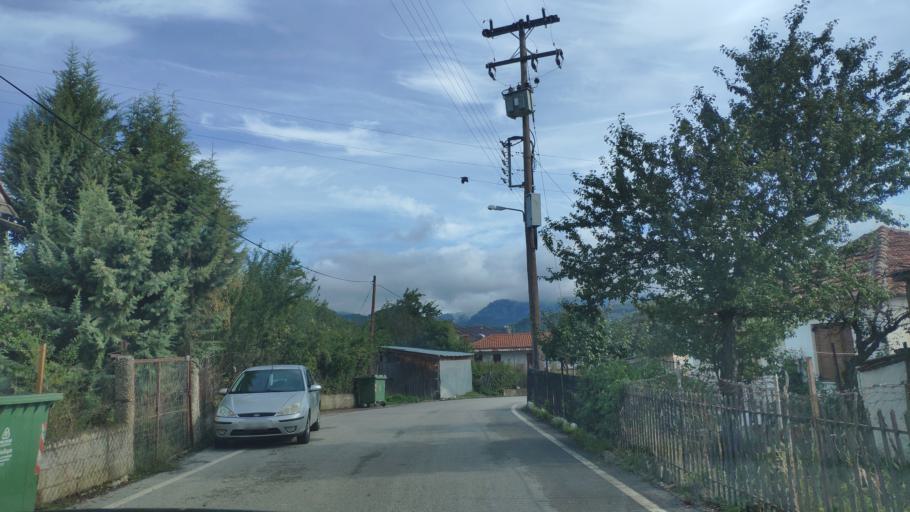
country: GR
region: West Macedonia
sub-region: Nomos Kastorias
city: Nestorio
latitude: 40.2739
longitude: 20.9746
